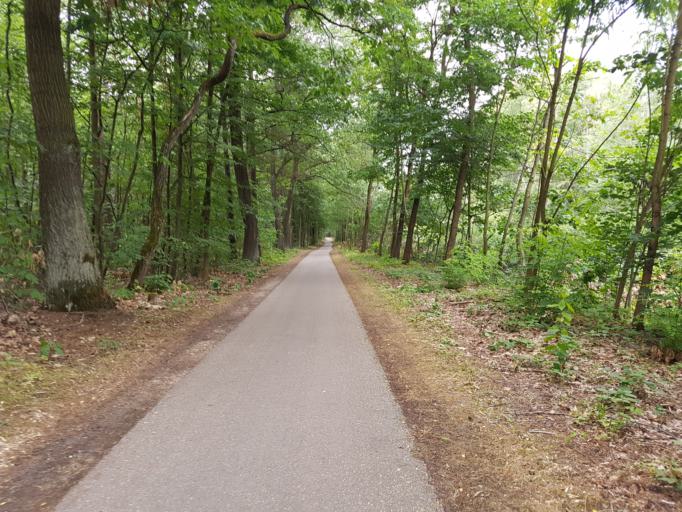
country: DE
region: Brandenburg
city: Finsterwalde
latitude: 51.6319
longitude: 13.6862
